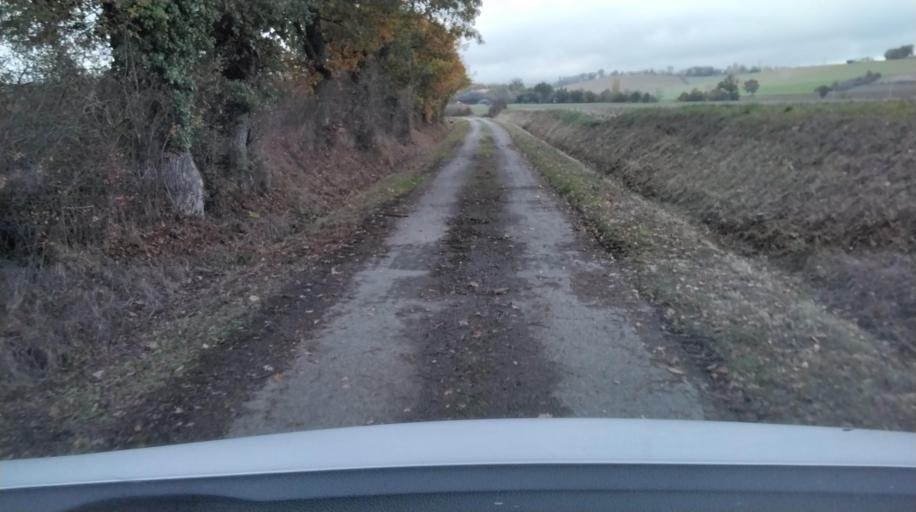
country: FR
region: Midi-Pyrenees
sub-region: Departement de la Haute-Garonne
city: Le Fousseret
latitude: 43.2701
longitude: 1.0311
